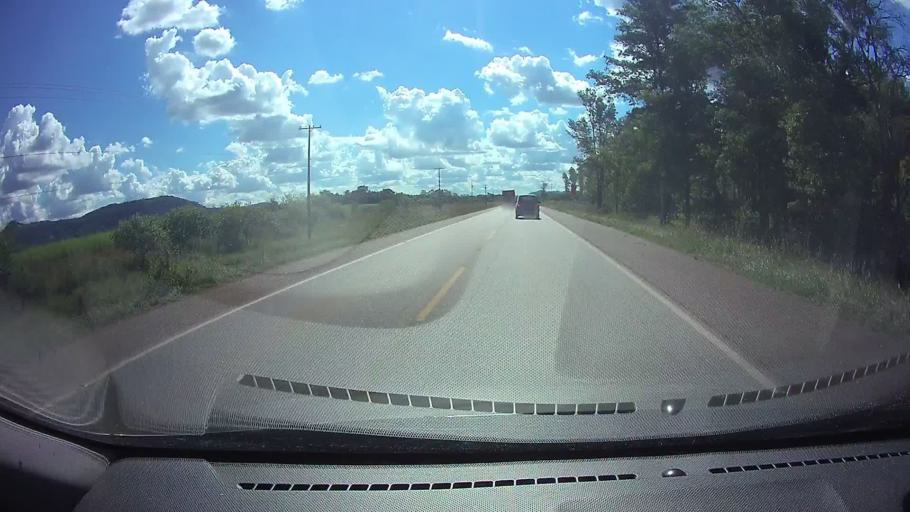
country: PY
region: Paraguari
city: La Colmena
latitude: -25.7543
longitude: -56.7729
